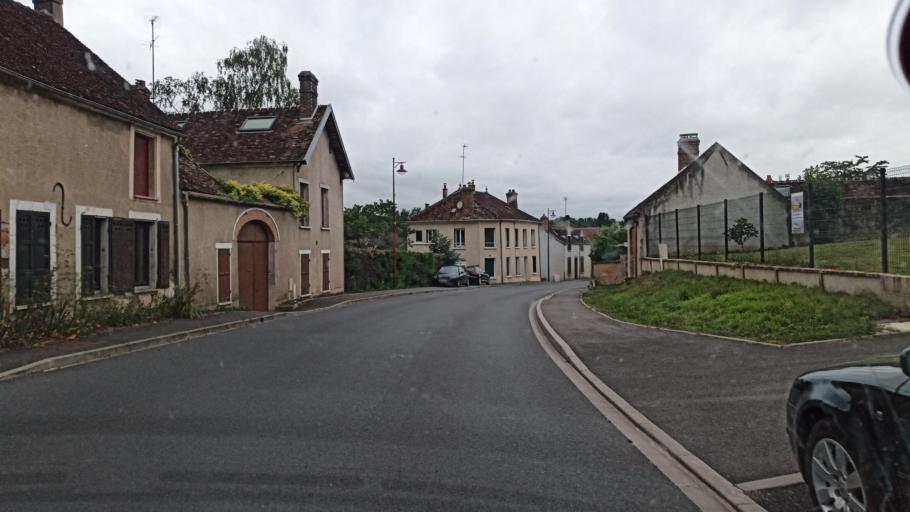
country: FR
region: Ile-de-France
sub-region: Departement de Seine-et-Marne
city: Voulx
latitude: 48.2854
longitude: 2.9608
